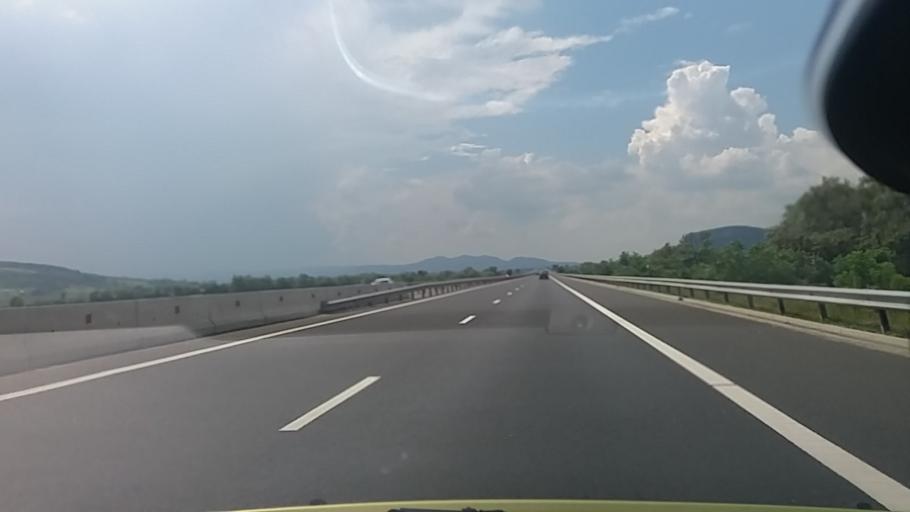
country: RO
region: Hunedoara
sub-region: Comuna Turdas
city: Turdas
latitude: 45.8391
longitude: 23.0921
